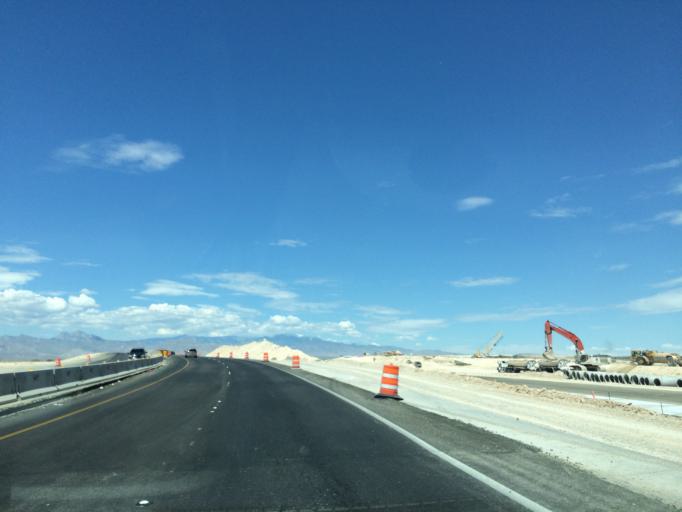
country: US
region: Nevada
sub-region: Clark County
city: North Las Vegas
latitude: 36.2932
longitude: -115.1473
